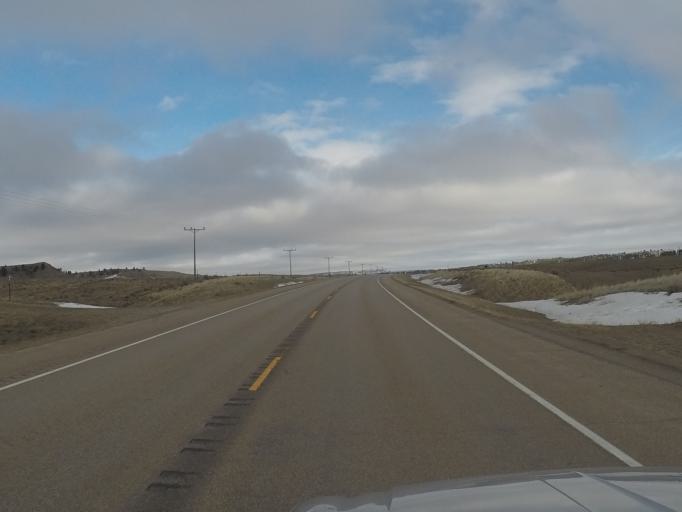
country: US
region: Montana
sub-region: Golden Valley County
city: Ryegate
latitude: 46.3104
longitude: -109.3598
